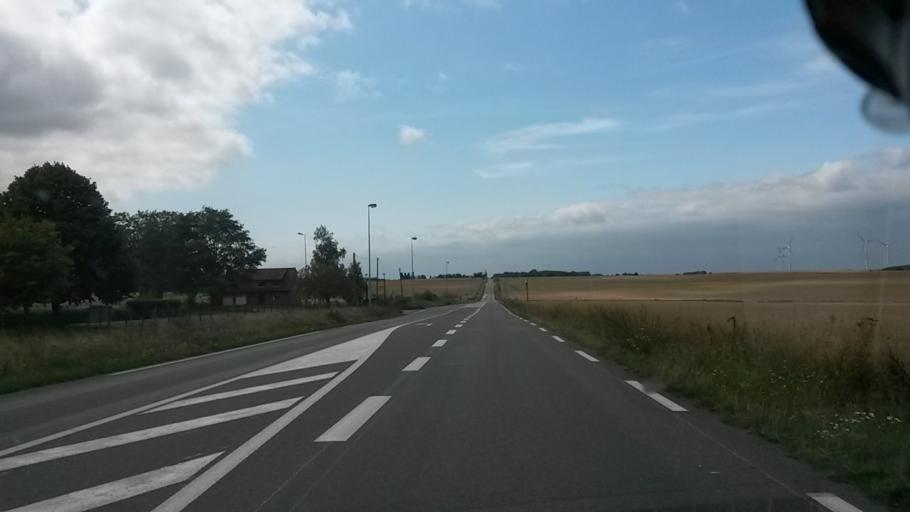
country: FR
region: Nord-Pas-de-Calais
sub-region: Departement du Pas-de-Calais
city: Hermies
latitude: 50.1453
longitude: 3.0577
